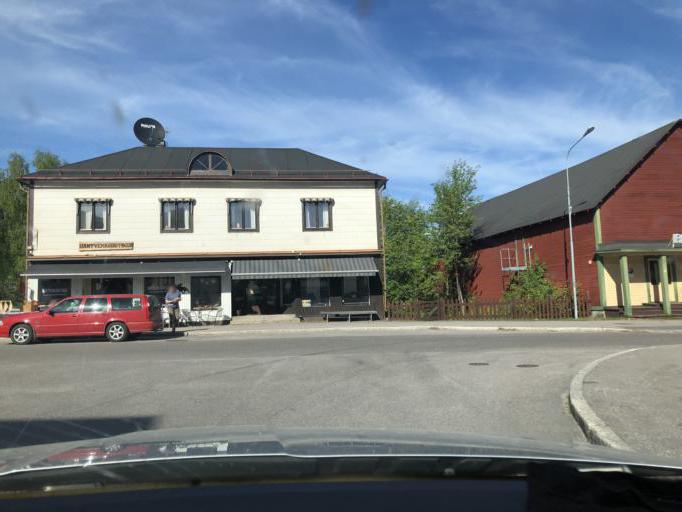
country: SE
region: Norrbotten
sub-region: Jokkmokks Kommun
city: Jokkmokk
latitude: 66.6069
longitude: 19.8320
